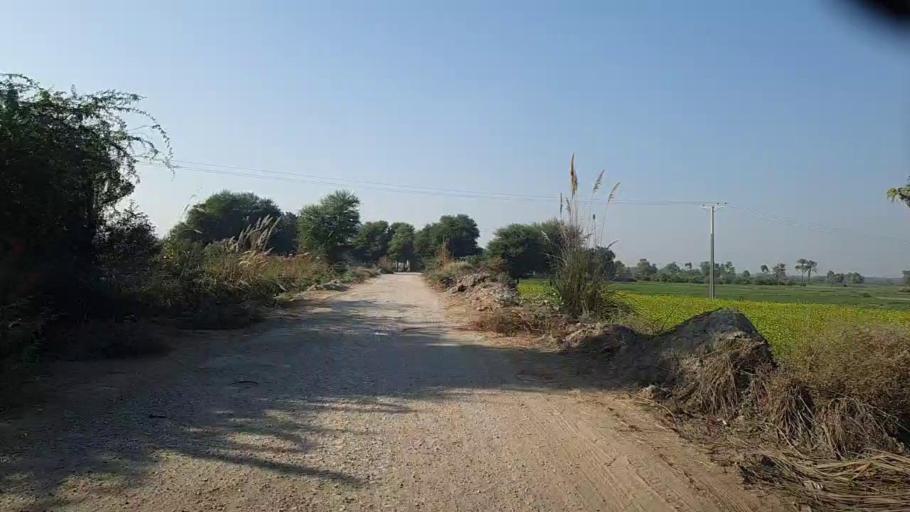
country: PK
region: Sindh
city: Darya Khan Marri
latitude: 26.6785
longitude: 68.3721
